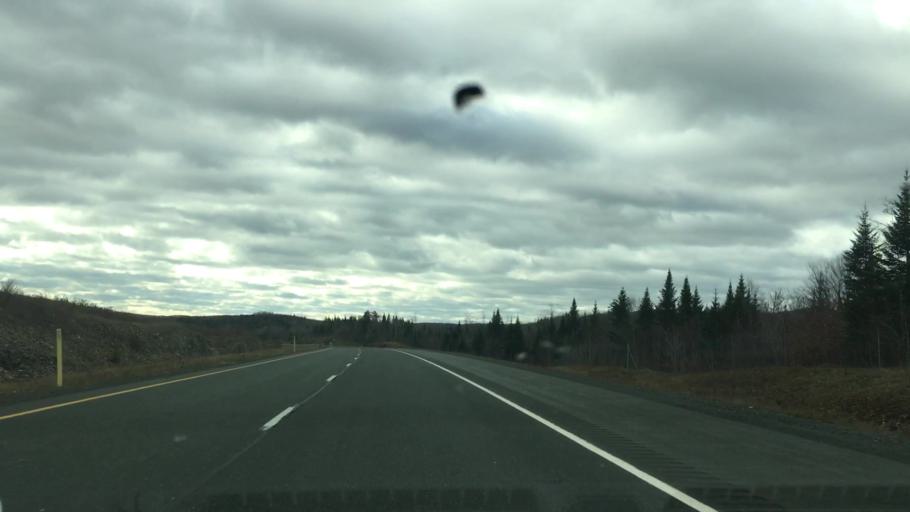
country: US
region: Maine
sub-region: Aroostook County
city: Easton
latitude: 46.6074
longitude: -67.7438
